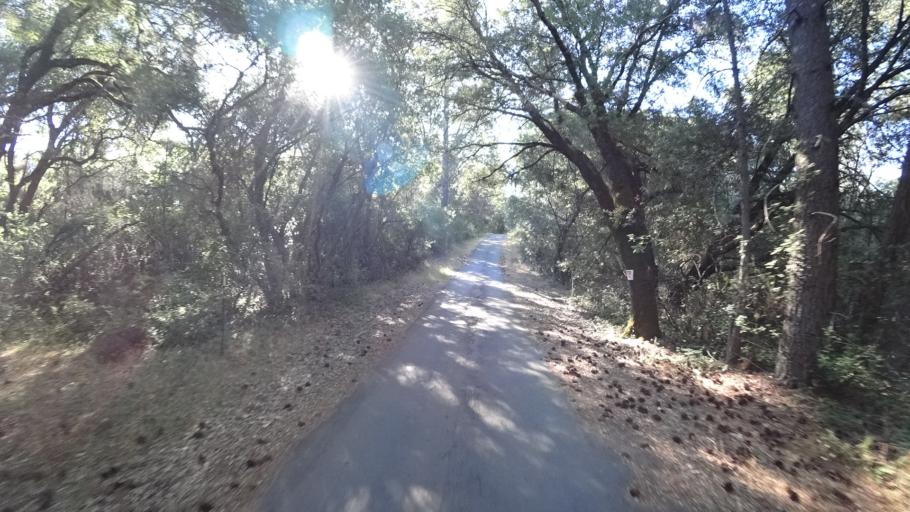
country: US
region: California
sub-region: Amador County
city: Pioneer
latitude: 38.3798
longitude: -120.5700
